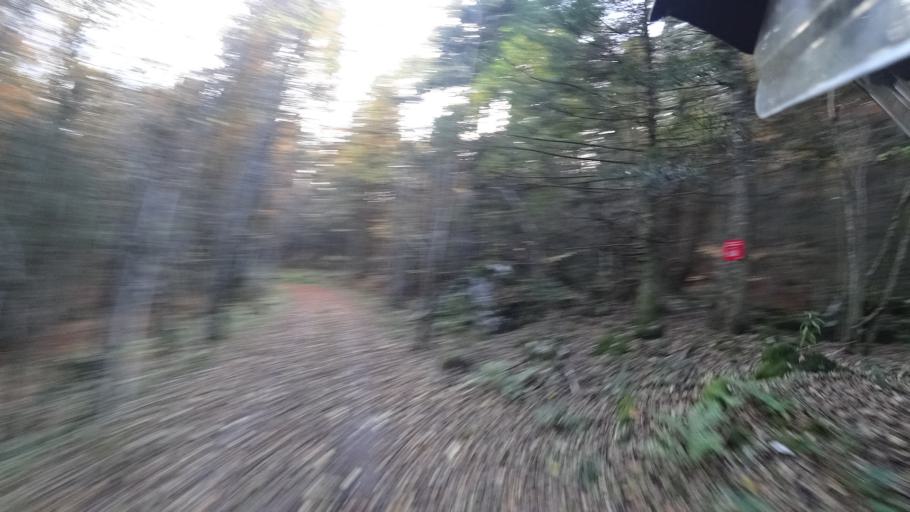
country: HR
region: Karlovacka
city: Plaski
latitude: 45.0409
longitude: 15.3221
